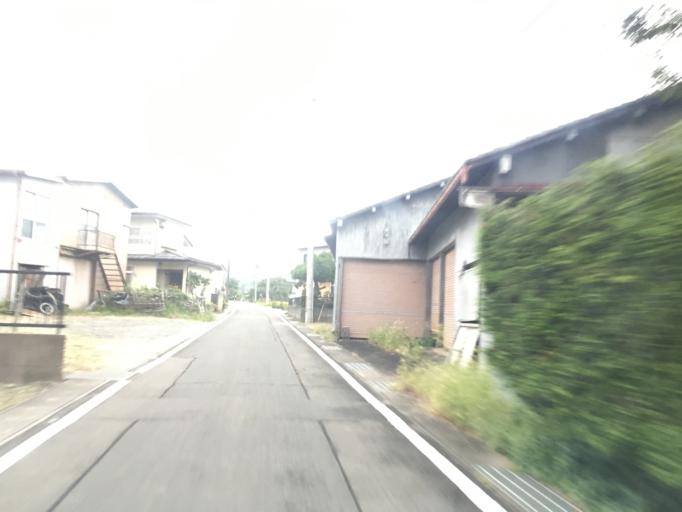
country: JP
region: Fukushima
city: Nihommatsu
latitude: 37.6526
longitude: 140.4550
